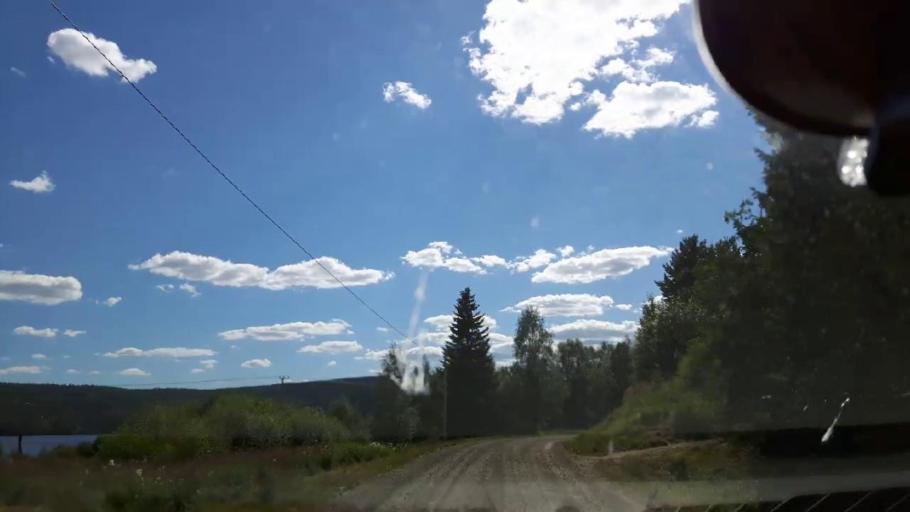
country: SE
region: Vaesternorrland
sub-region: Ange Kommun
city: Fransta
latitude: 62.7944
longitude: 16.1891
